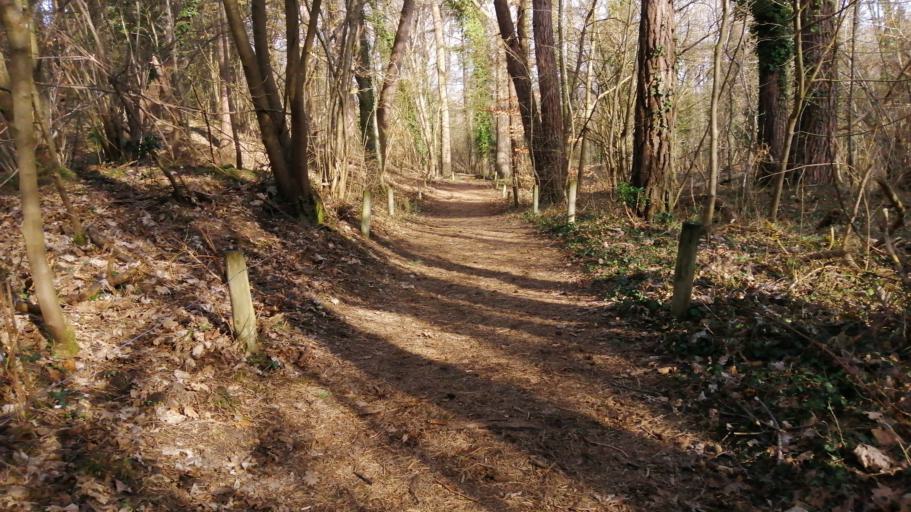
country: FR
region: Nord-Pas-de-Calais
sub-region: Departement du Pas-de-Calais
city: Dannes
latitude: 50.5969
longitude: 1.6090
